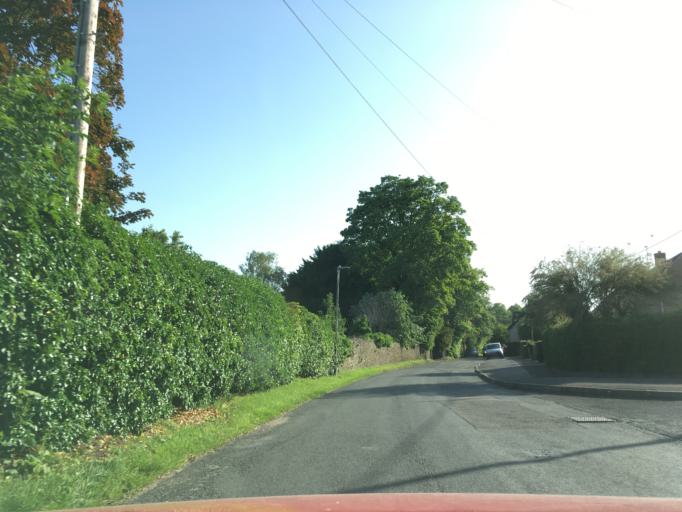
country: GB
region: England
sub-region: Gloucestershire
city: Fairford
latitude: 51.7097
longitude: -1.7732
